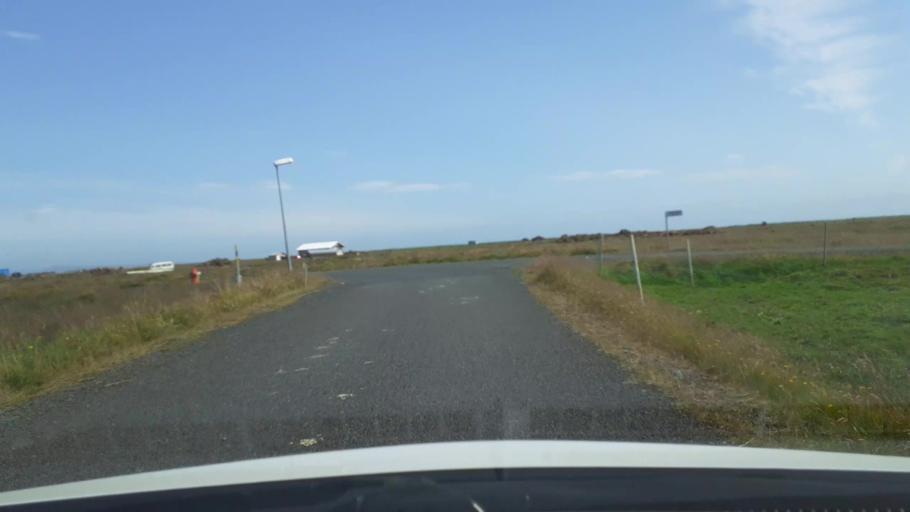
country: IS
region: South
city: Selfoss
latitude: 63.8891
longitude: -21.0870
